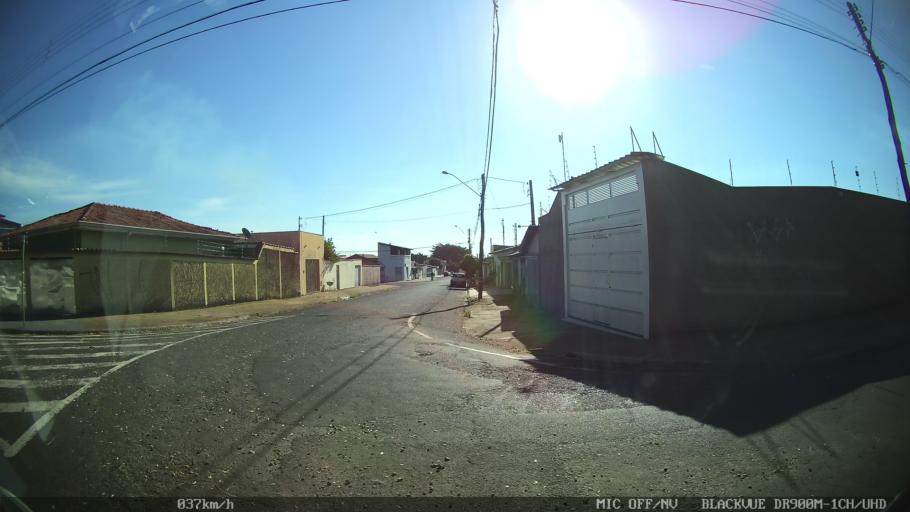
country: BR
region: Sao Paulo
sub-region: Franca
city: Franca
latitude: -20.5006
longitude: -47.4167
